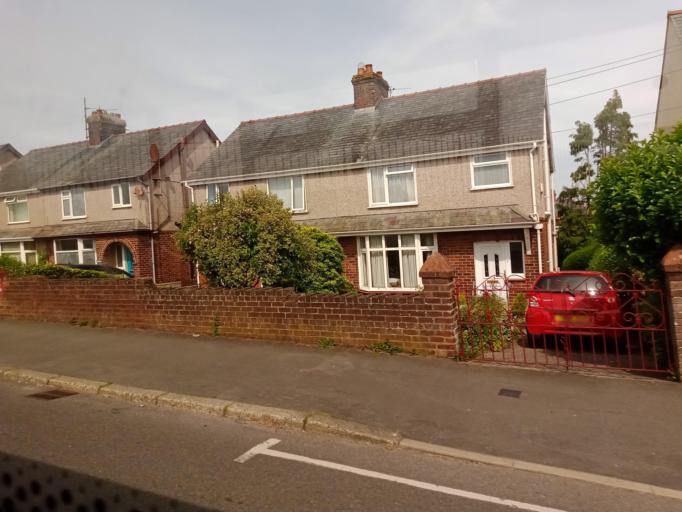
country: GB
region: Wales
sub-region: Gwynedd
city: Bangor
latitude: 53.2217
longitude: -4.1462
